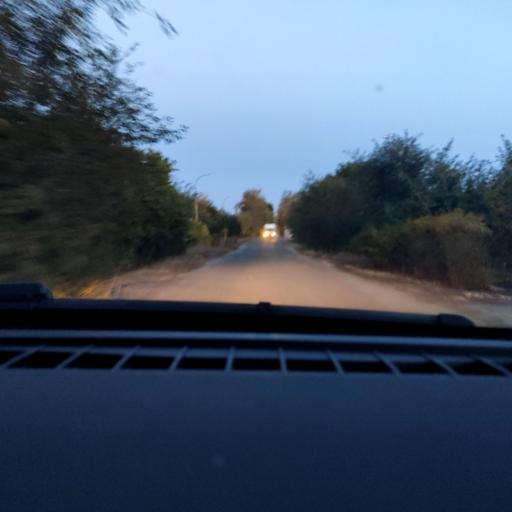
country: RU
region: Voronezj
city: Maslovka
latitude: 51.6158
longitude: 39.2656
